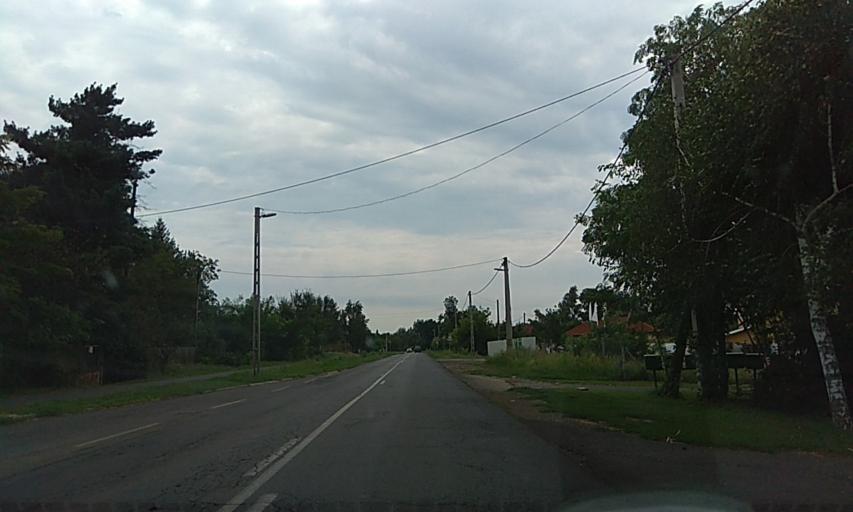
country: HU
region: Szabolcs-Szatmar-Bereg
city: Kotaj
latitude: 48.0079
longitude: 21.6951
